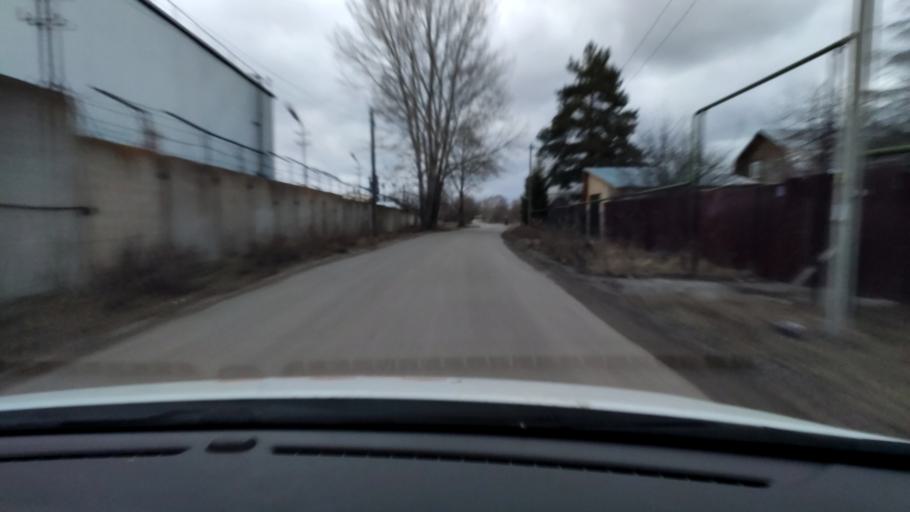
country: RU
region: Tatarstan
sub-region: Gorod Kazan'
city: Kazan
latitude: 55.7225
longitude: 49.0985
